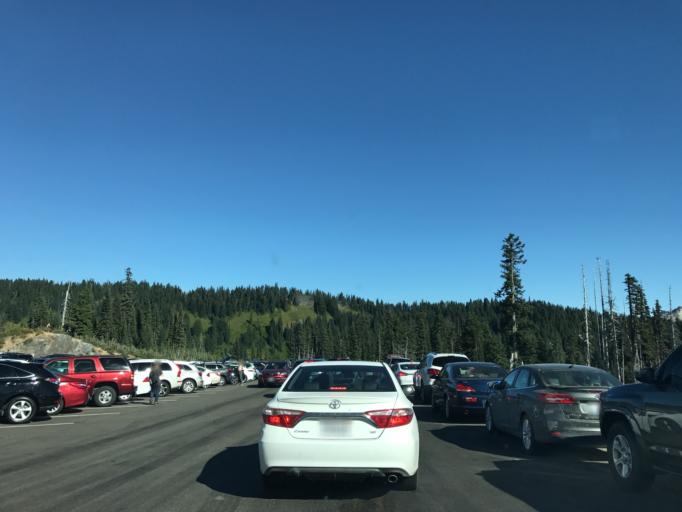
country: US
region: Washington
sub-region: Pierce County
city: Buckley
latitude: 46.7855
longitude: -121.7361
